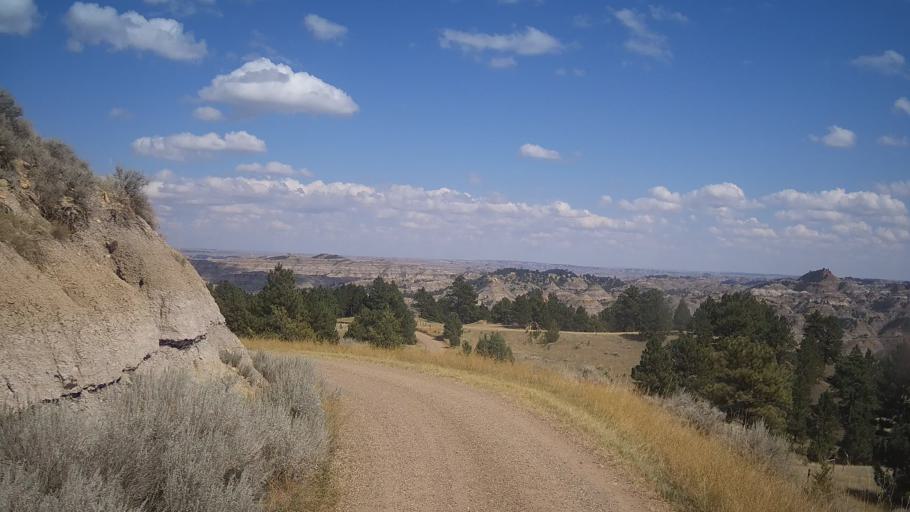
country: US
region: Montana
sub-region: Dawson County
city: Glendive
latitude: 47.0576
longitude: -104.6684
